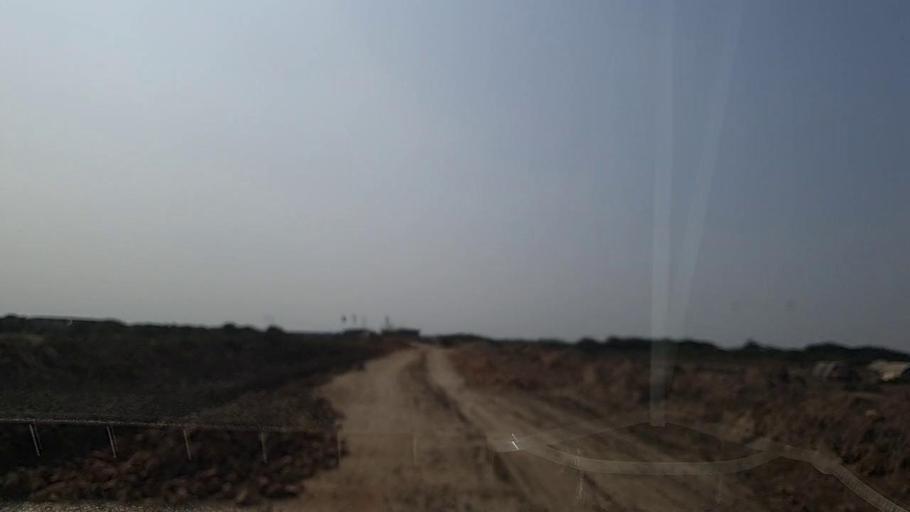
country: PK
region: Sindh
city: Chuhar Jamali
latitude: 24.1927
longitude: 67.8476
